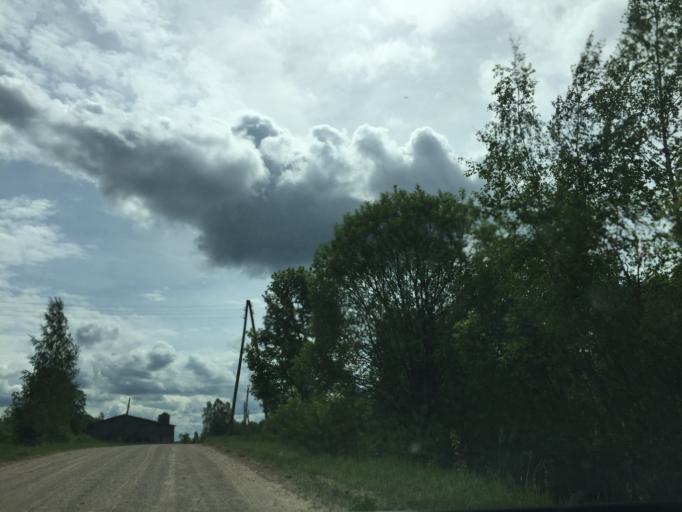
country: LV
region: Dagda
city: Dagda
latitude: 56.0325
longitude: 27.6253
